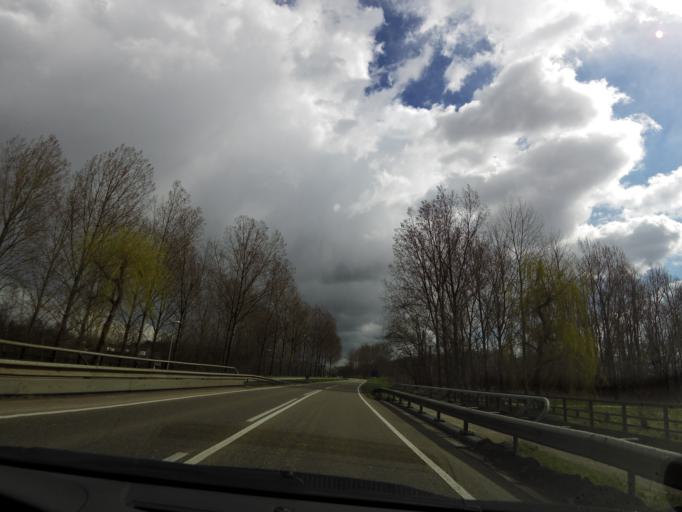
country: NL
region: Limburg
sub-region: Gemeente Sittard-Geleen
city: Sittard
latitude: 50.9821
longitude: 5.8616
